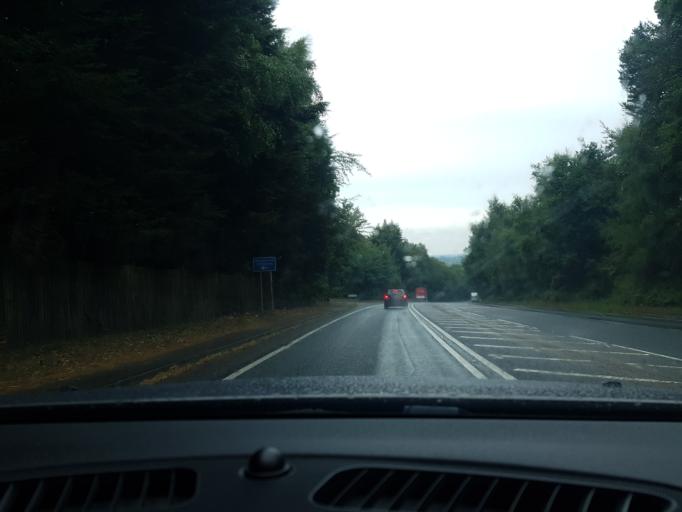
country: GB
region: England
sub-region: Surrey
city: Farnham
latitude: 51.2377
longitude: -0.8352
